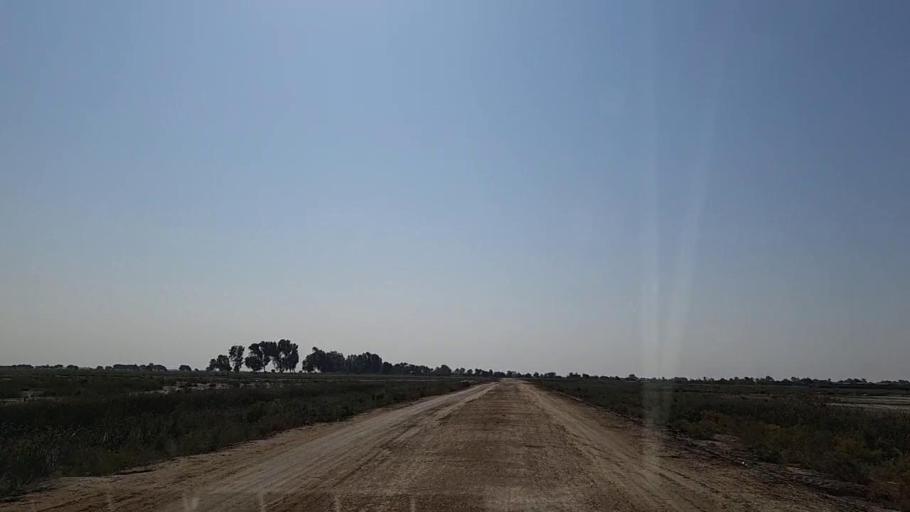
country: PK
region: Sindh
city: Chuhar Jamali
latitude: 24.5020
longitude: 68.0984
